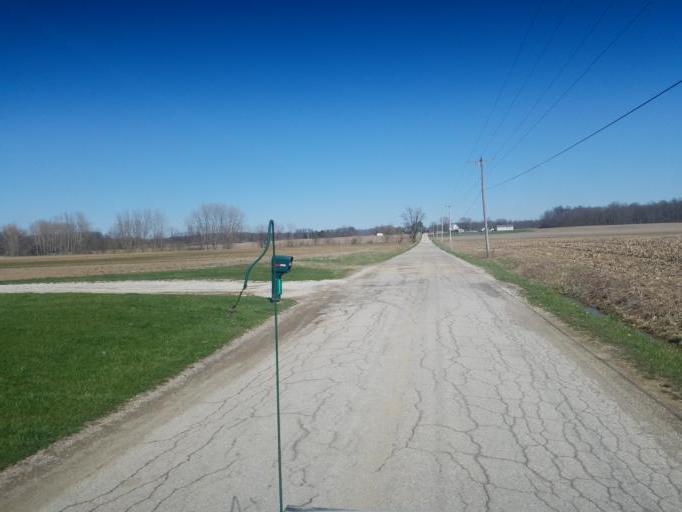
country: US
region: Ohio
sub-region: Morrow County
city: Mount Gilead
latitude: 40.5865
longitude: -82.8907
